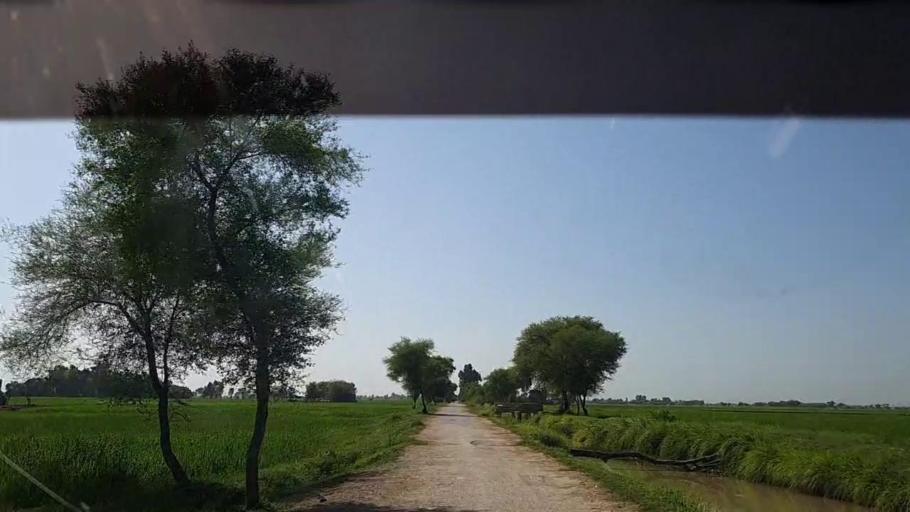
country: PK
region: Sindh
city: Ghauspur
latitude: 28.1766
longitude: 69.0434
